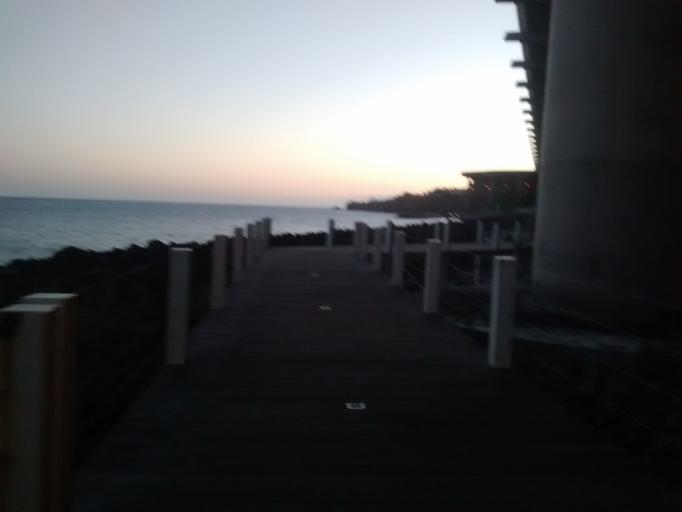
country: PT
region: Madeira
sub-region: Machico
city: Machico
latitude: 32.7052
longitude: -16.7648
